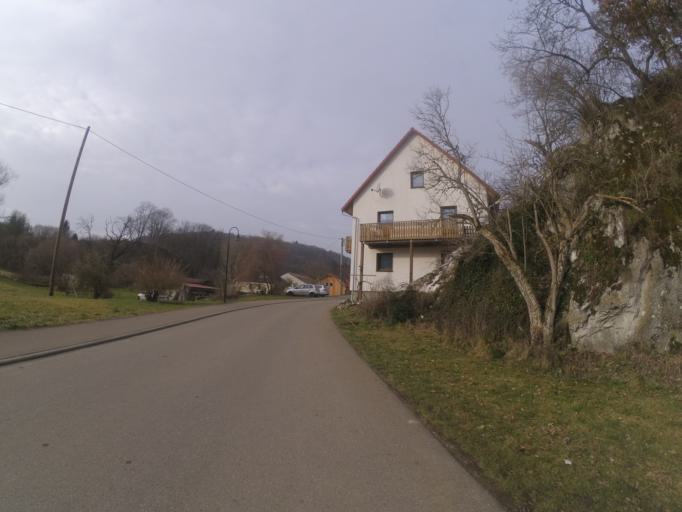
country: DE
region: Baden-Wuerttemberg
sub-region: Tuebingen Region
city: Hayingen
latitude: 48.2910
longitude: 9.5045
